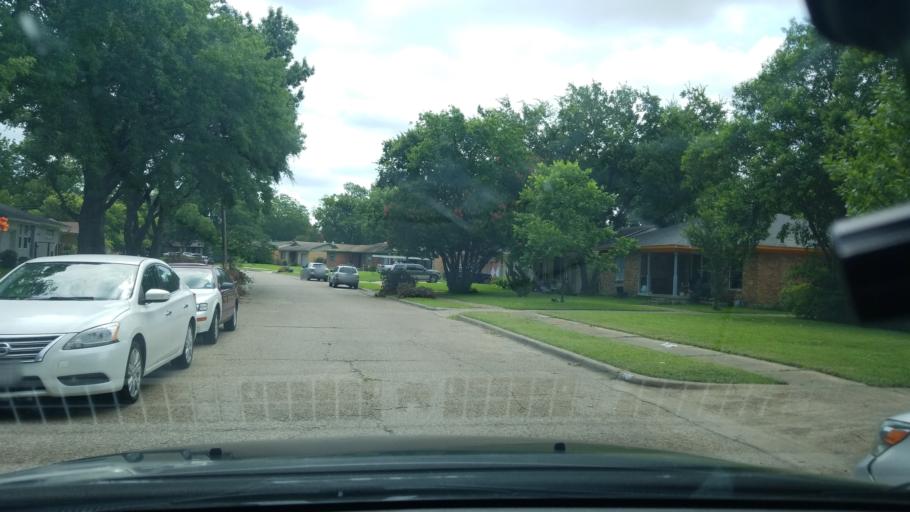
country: US
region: Texas
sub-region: Dallas County
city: Garland
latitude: 32.8286
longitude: -96.6748
